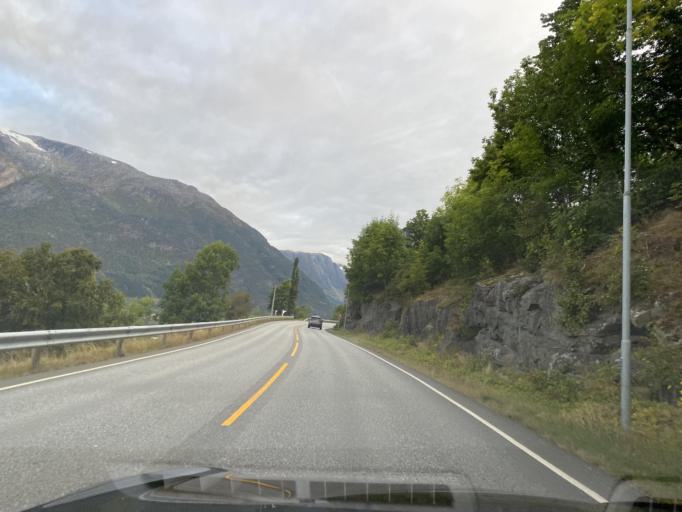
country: NO
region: Hordaland
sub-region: Odda
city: Odda
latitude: 60.1859
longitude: 6.5901
